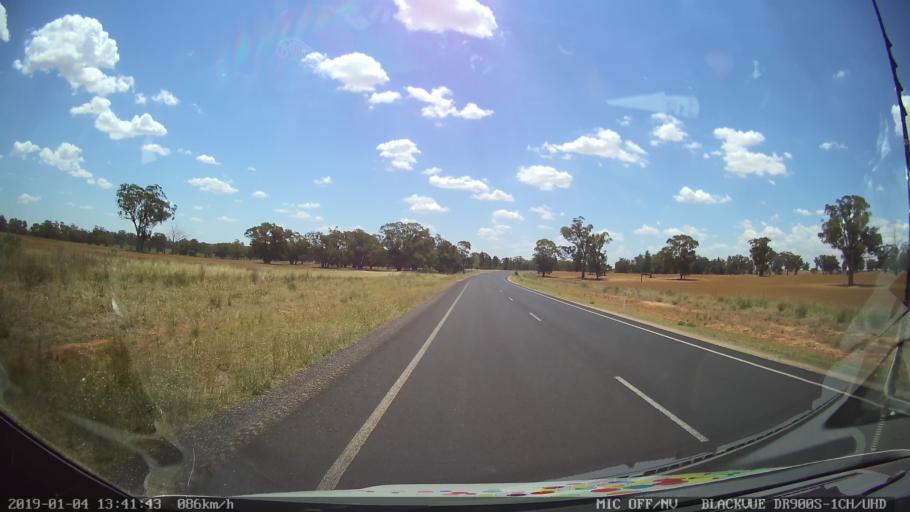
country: AU
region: New South Wales
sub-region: Dubbo Municipality
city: Dubbo
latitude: -32.4989
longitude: 148.5533
